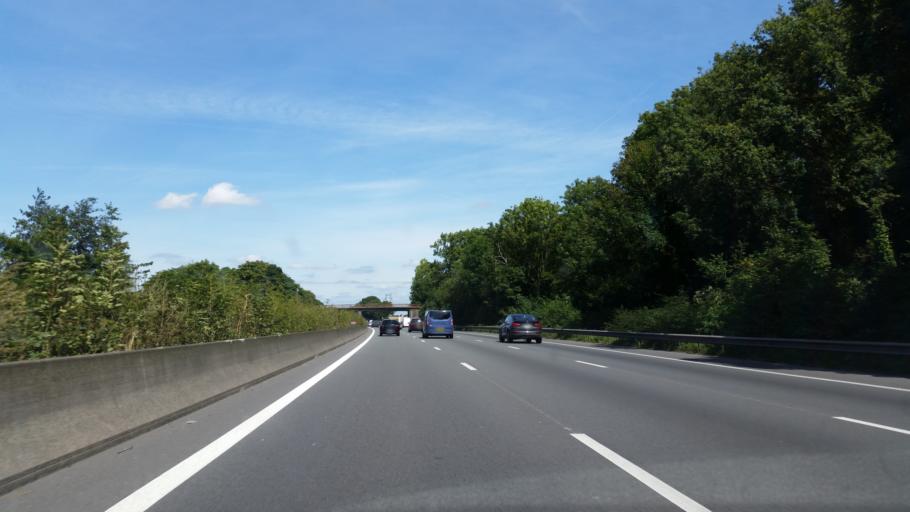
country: FR
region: Nord-Pas-de-Calais
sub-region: Departement du Nord
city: Phalempin
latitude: 50.5161
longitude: 3.0359
